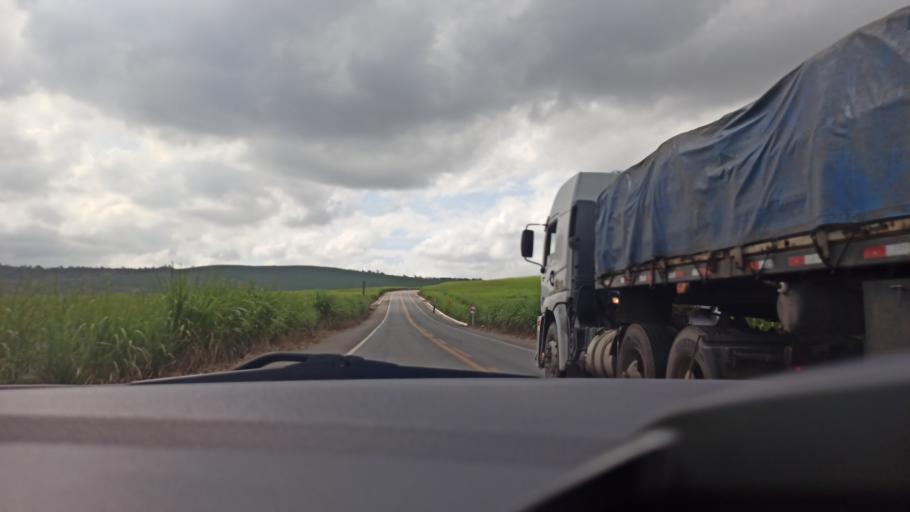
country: BR
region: Pernambuco
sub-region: Timbauba
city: Timbauba
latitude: -7.5249
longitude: -35.2914
